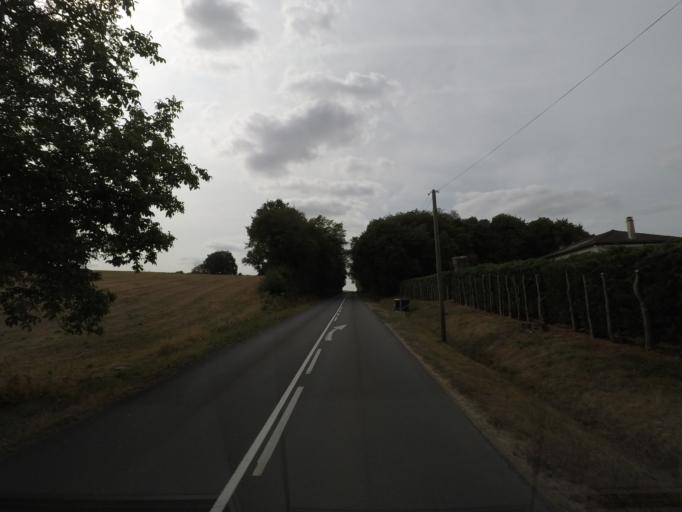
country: FR
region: Poitou-Charentes
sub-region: Departement de la Charente
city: Nanteuil-en-Vallee
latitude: 45.9860
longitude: 0.3490
